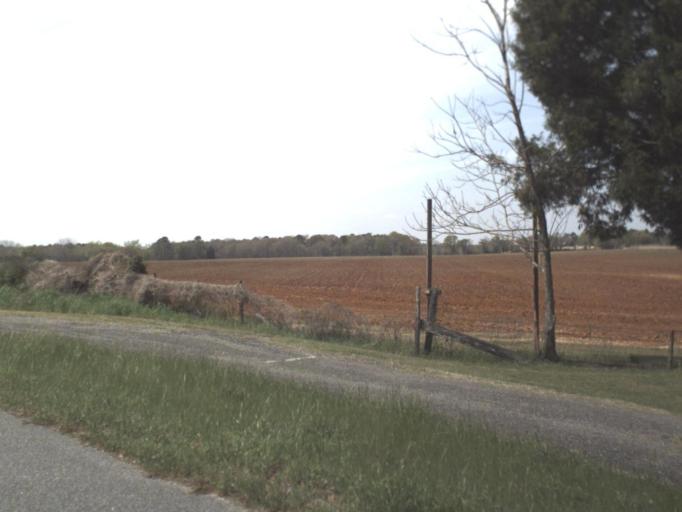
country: US
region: Florida
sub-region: Jackson County
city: Graceville
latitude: 30.9852
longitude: -85.4840
